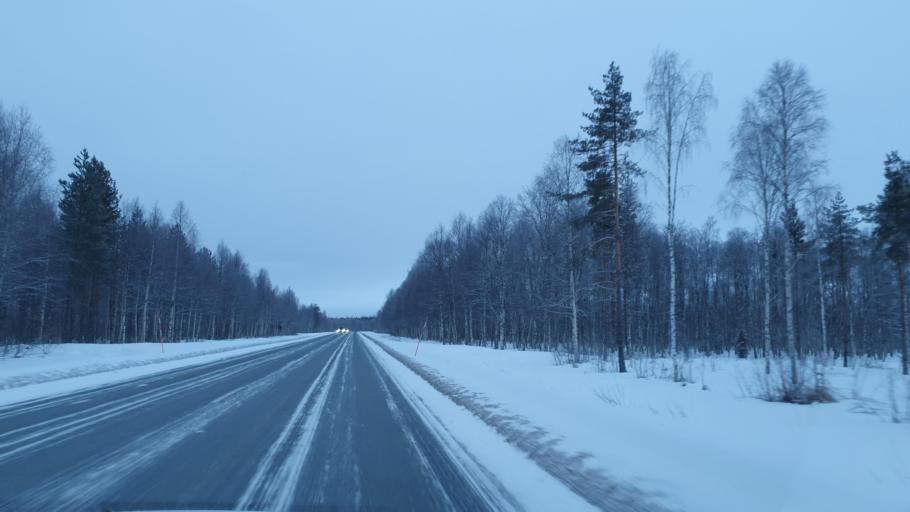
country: SE
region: Norrbotten
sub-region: Overtornea Kommun
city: OEvertornea
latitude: 66.4516
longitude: 23.6948
